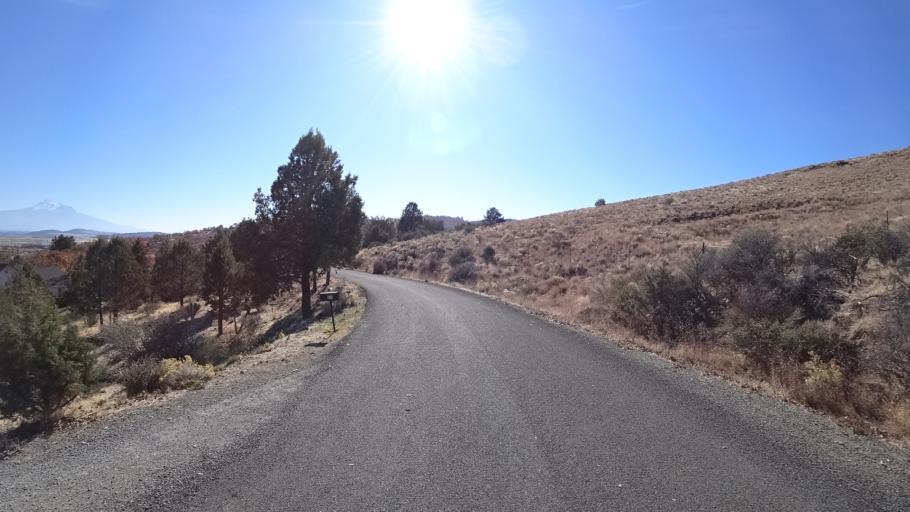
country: US
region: California
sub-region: Siskiyou County
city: Yreka
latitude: 41.7435
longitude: -122.6125
